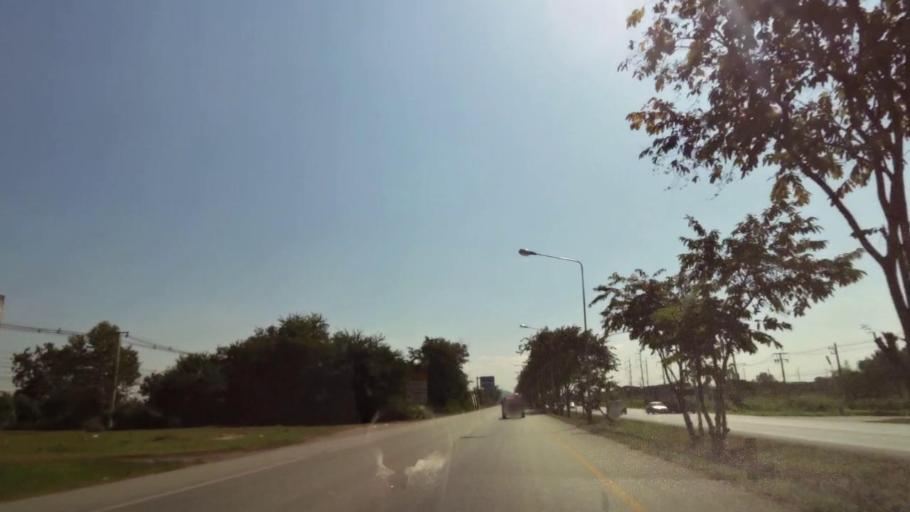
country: TH
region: Nakhon Sawan
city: Nakhon Sawan
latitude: 15.7723
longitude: 100.1213
